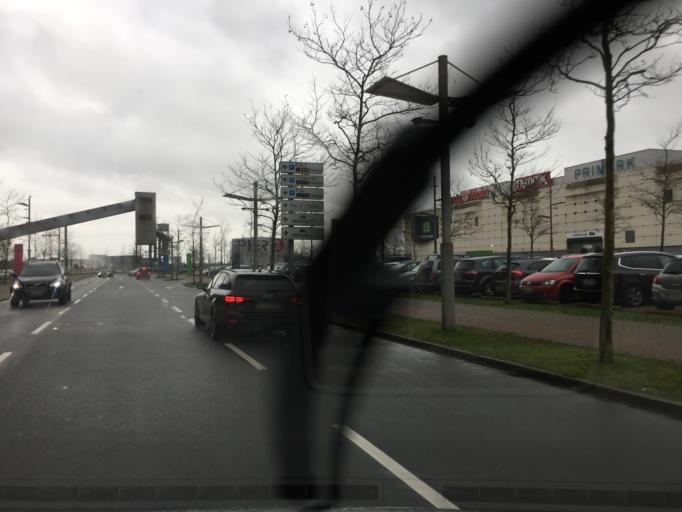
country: DE
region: Bremen
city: Bremen
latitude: 53.1107
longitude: 8.7512
